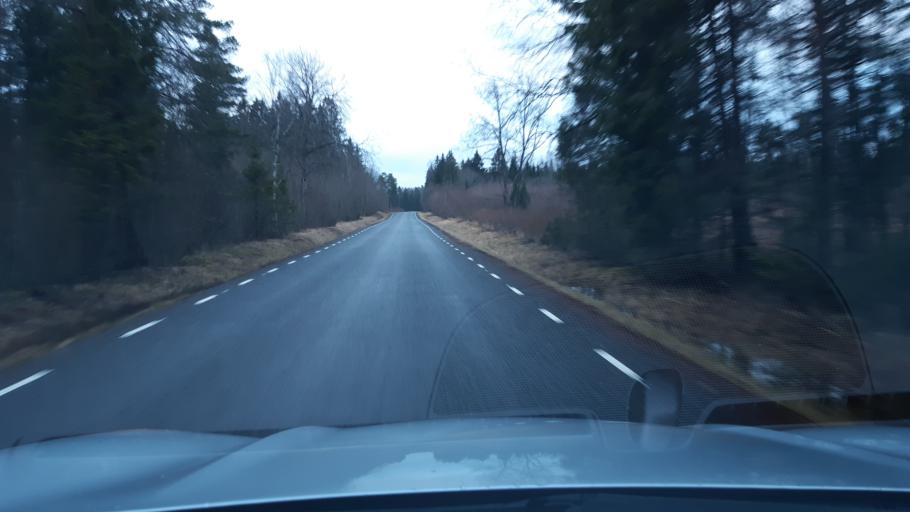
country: EE
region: Harju
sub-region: Saku vald
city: Saku
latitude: 59.1837
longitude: 24.6082
